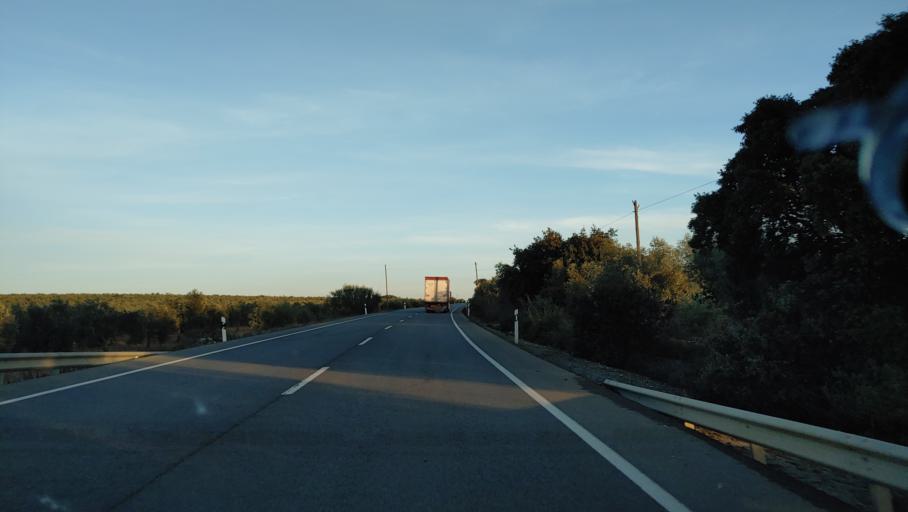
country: ES
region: Andalusia
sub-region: Provincia de Malaga
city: Humilladero
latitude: 37.0582
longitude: -4.6813
